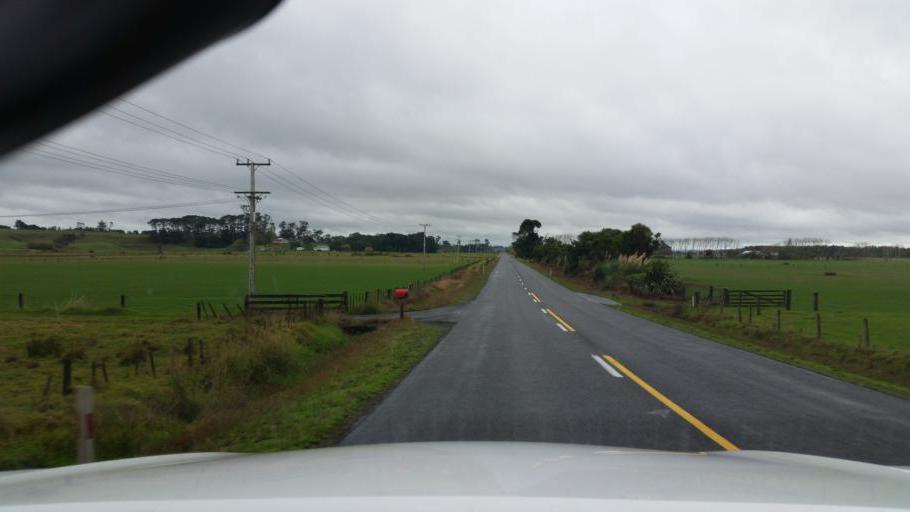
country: NZ
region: Northland
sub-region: Kaipara District
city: Dargaville
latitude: -36.0746
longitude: 173.9453
